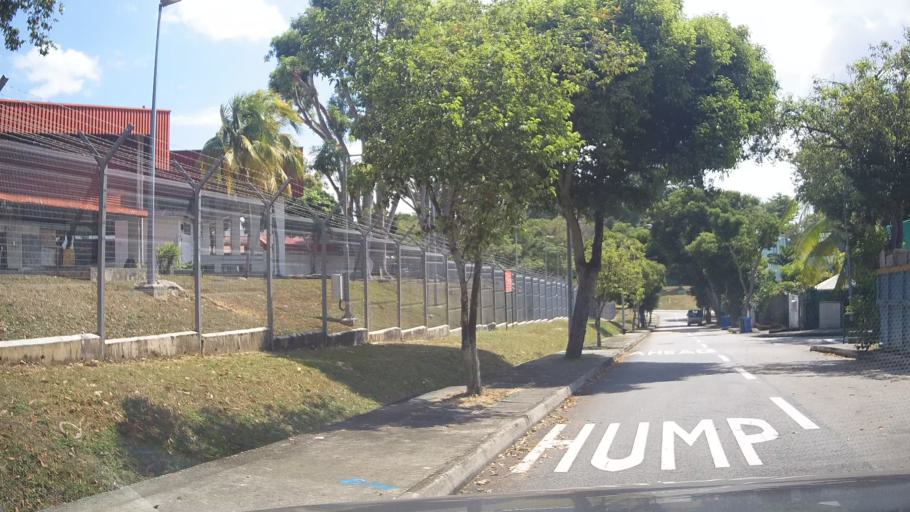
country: MY
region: Johor
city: Kampung Pasir Gudang Baru
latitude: 1.3663
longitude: 103.9743
